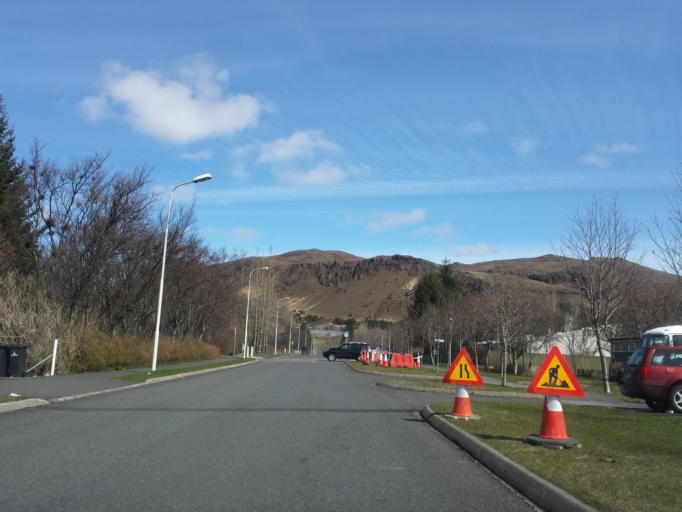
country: IS
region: South
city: Hveragerdi
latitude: 63.9975
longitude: -21.1842
